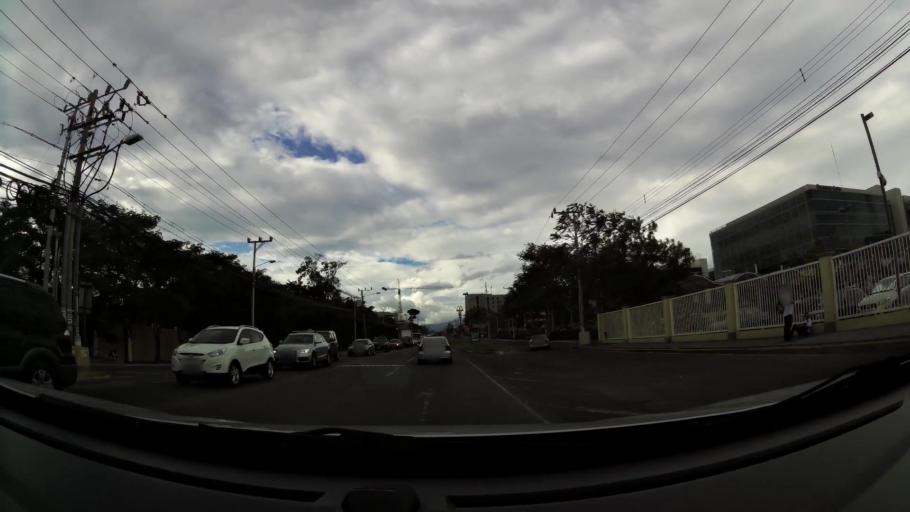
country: CR
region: San Jose
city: Santa Ana
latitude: 9.9541
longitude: -84.1946
